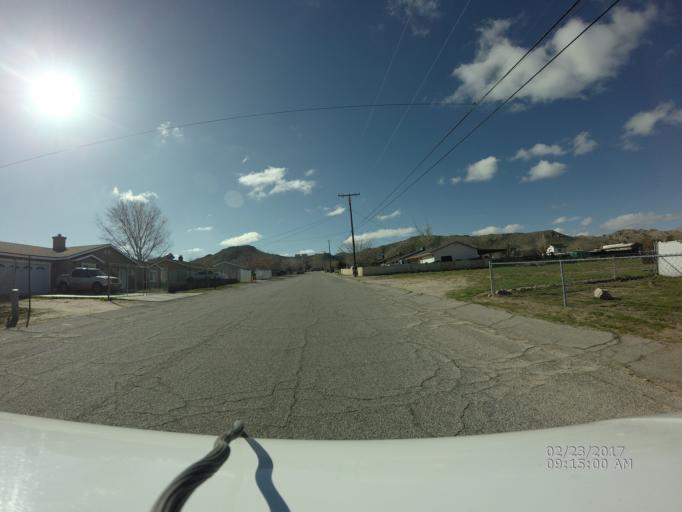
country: US
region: California
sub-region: Los Angeles County
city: Lake Los Angeles
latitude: 34.6142
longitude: -117.8404
